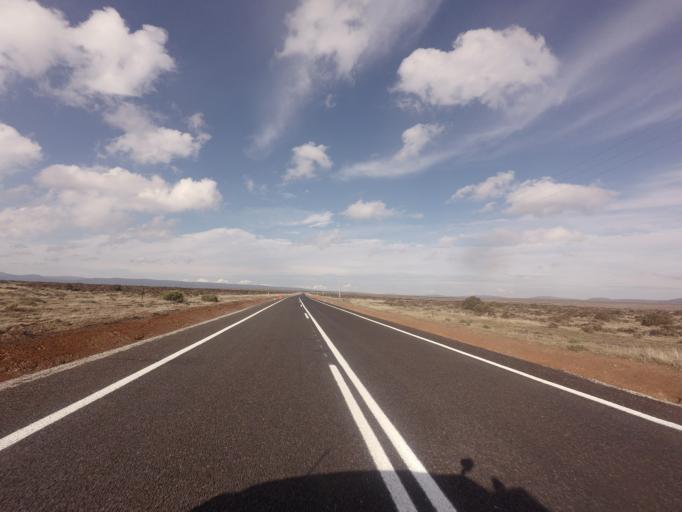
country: AU
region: Tasmania
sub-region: Meander Valley
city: Deloraine
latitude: -41.9082
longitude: 146.6752
